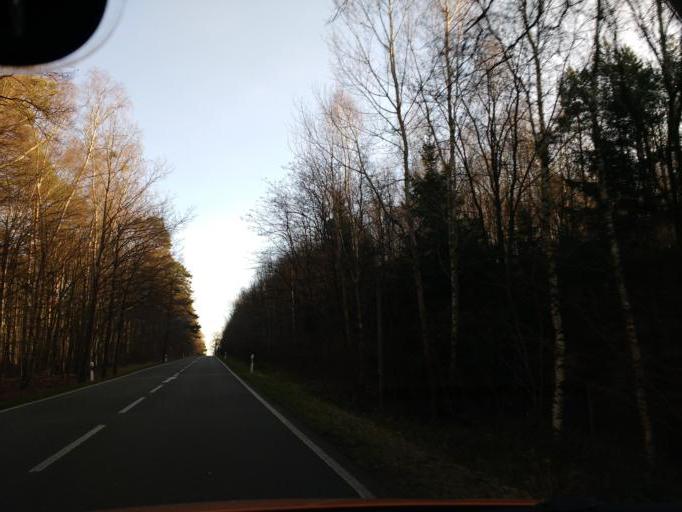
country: DE
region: Brandenburg
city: Protzel
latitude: 52.6447
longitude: 13.9448
